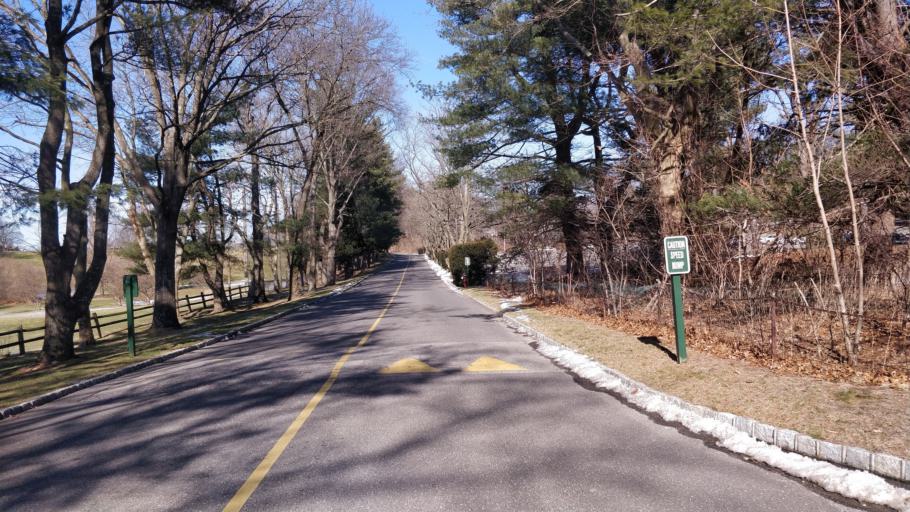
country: US
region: New York
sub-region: Nassau County
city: Old Westbury
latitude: 40.7991
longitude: -73.5983
